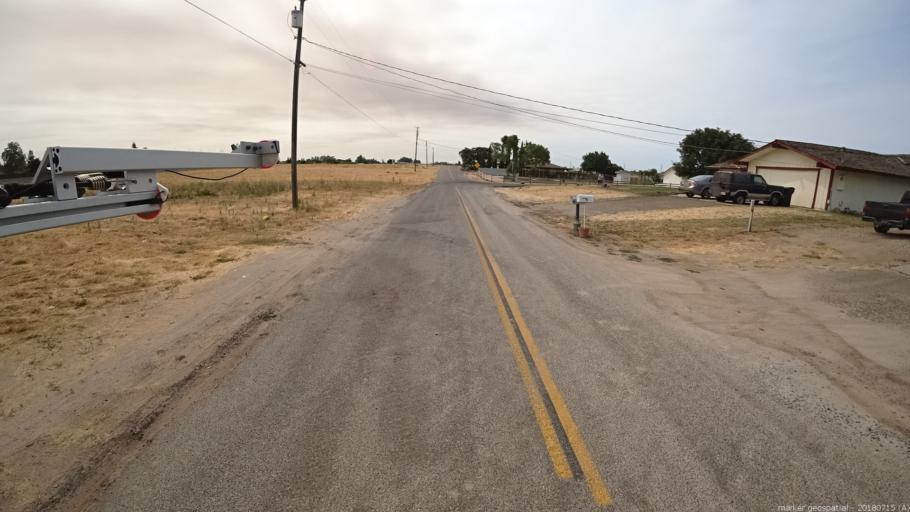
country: US
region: California
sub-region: Madera County
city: Madera Acres
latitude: 37.0158
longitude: -120.0684
